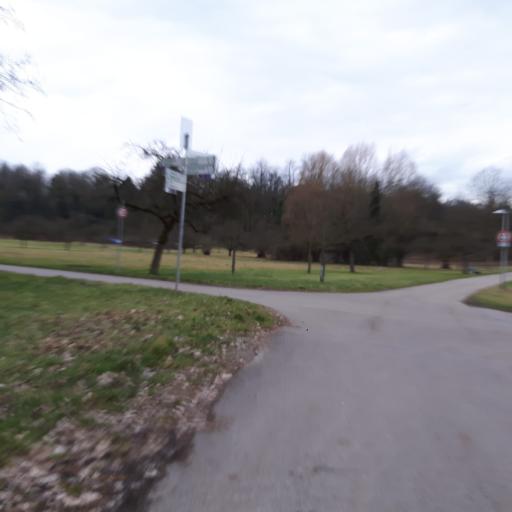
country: DE
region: Baden-Wuerttemberg
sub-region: Regierungsbezirk Stuttgart
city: Marbach am Neckar
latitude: 48.9419
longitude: 9.2510
